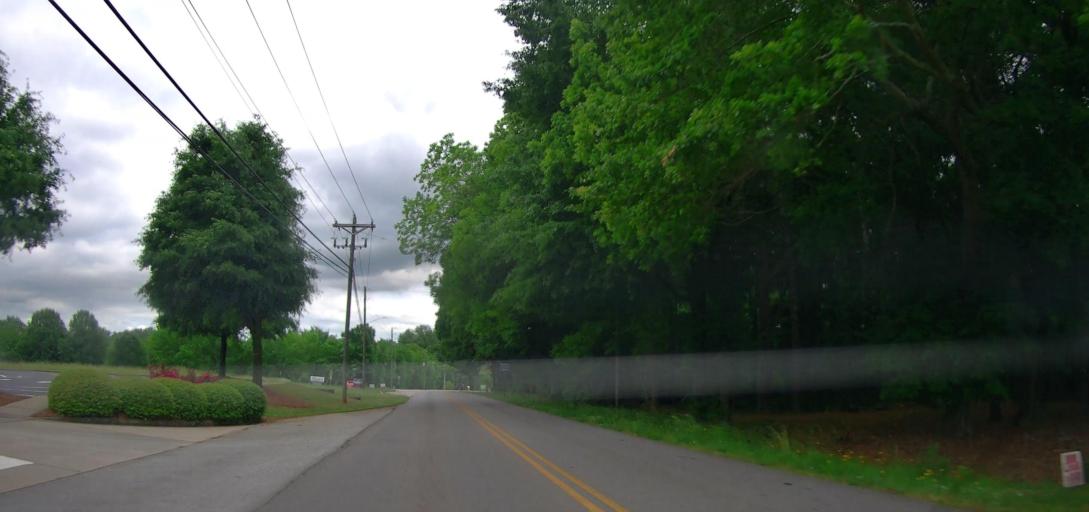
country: US
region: Georgia
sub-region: Walton County
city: Monroe
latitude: 33.7989
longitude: -83.6994
